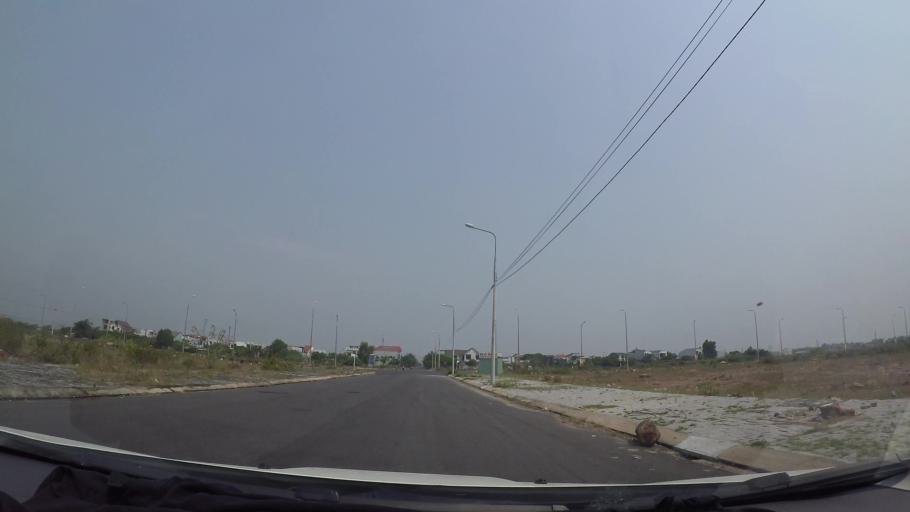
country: VN
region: Da Nang
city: Cam Le
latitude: 15.9769
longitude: 108.2143
